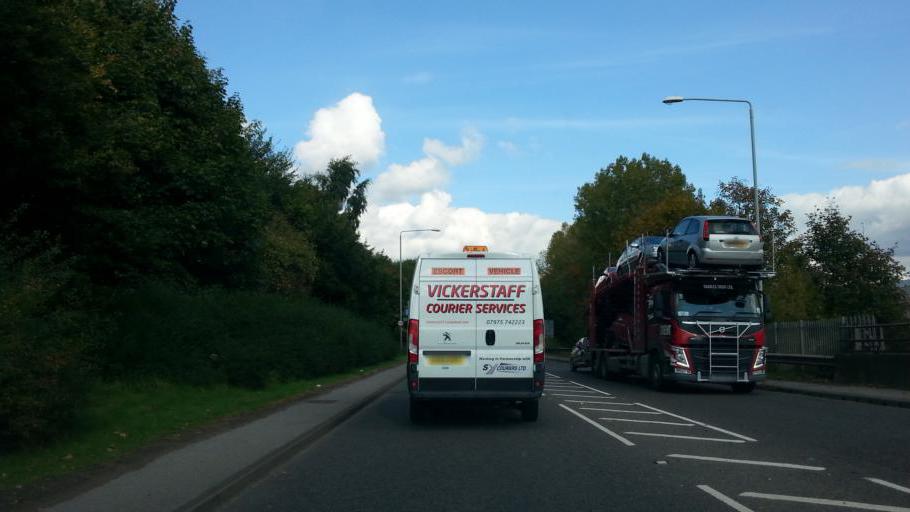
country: GB
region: England
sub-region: Nottinghamshire
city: Sutton in Ashfield
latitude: 53.1225
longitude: -1.2483
